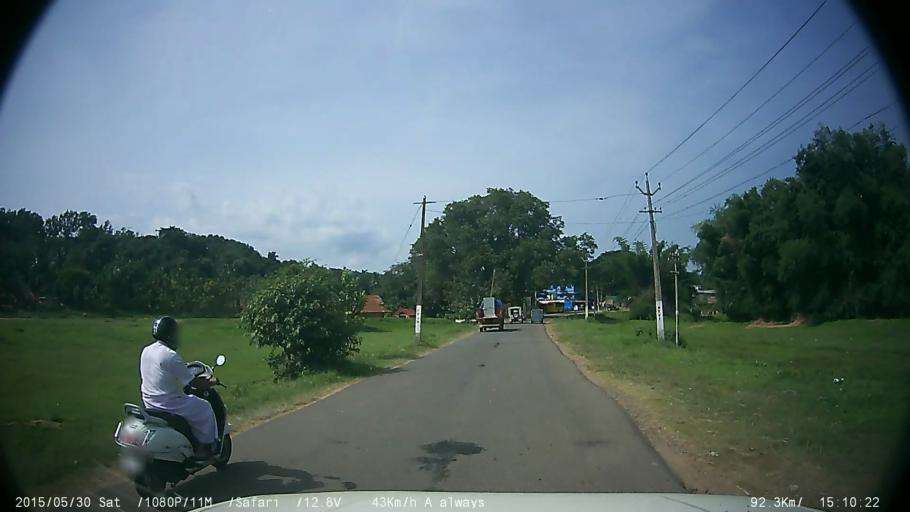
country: IN
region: Kerala
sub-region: Wayanad
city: Panamaram
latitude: 11.8012
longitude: 76.0293
